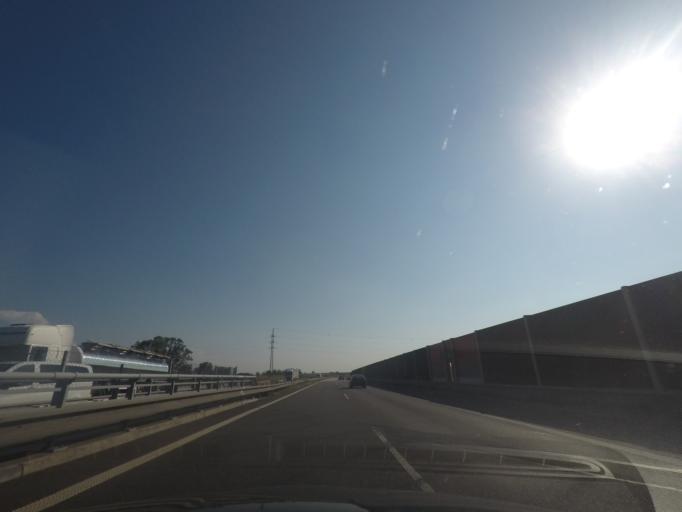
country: CZ
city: Bilovec
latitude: 49.7121
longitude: 17.9995
